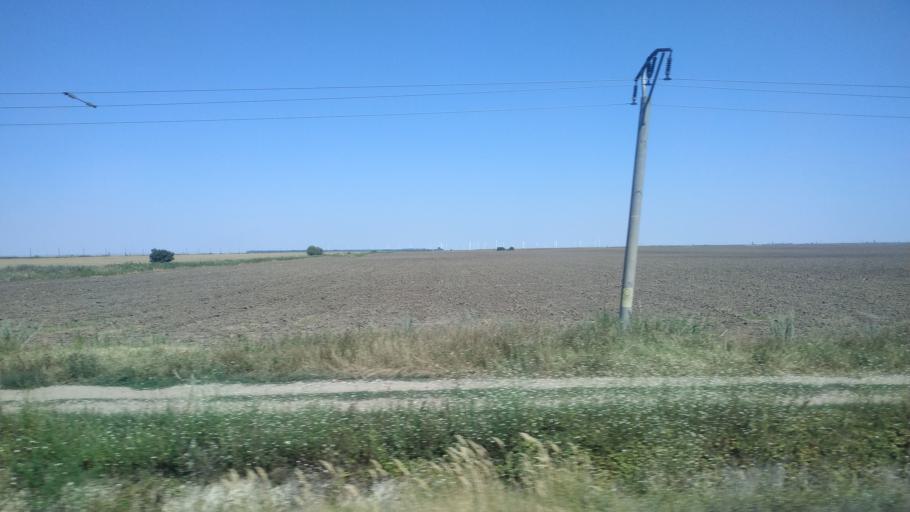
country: RO
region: Ialomita
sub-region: Municipiul Fetesti
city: Buliga
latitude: 44.4192
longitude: 27.7344
